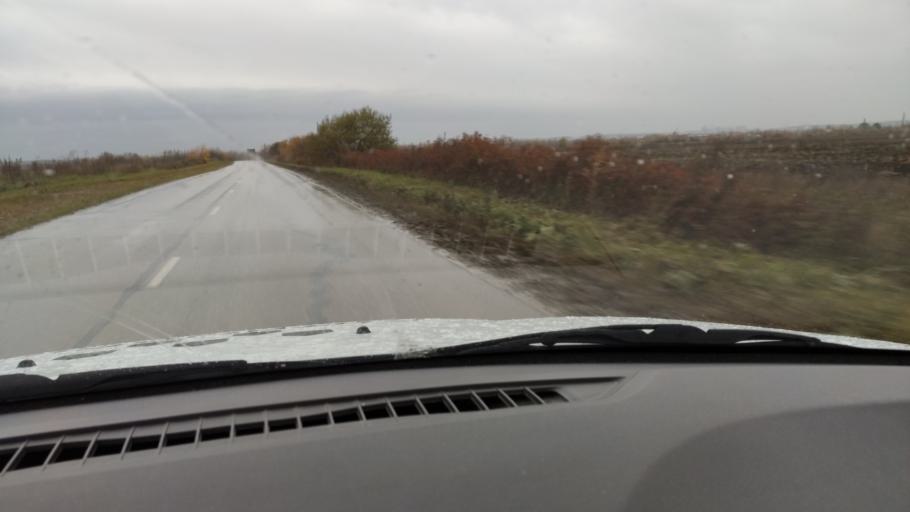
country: RU
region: Perm
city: Kondratovo
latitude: 57.9929
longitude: 56.0907
